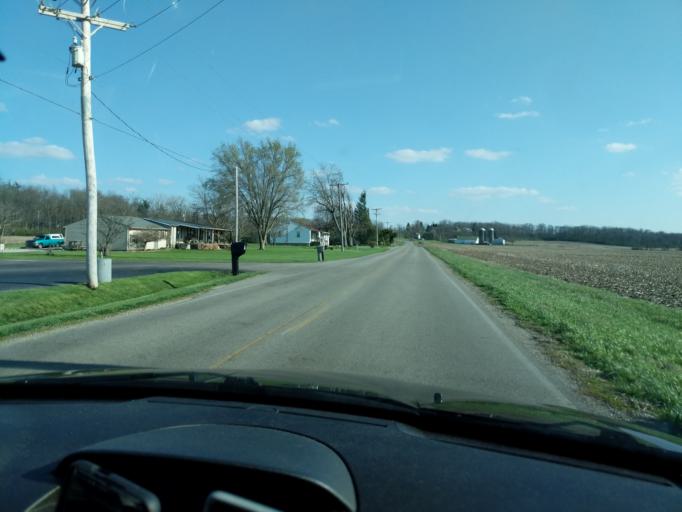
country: US
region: Ohio
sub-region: Champaign County
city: Urbana
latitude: 40.1071
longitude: -83.6679
